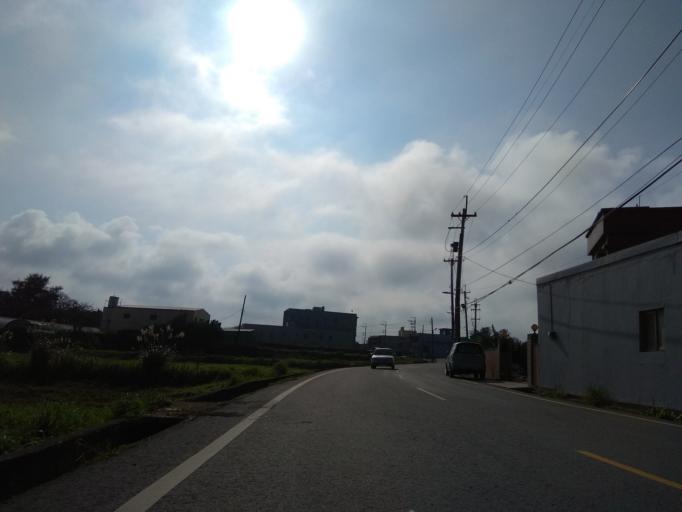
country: TW
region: Taiwan
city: Taoyuan City
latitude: 25.0783
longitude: 121.1712
